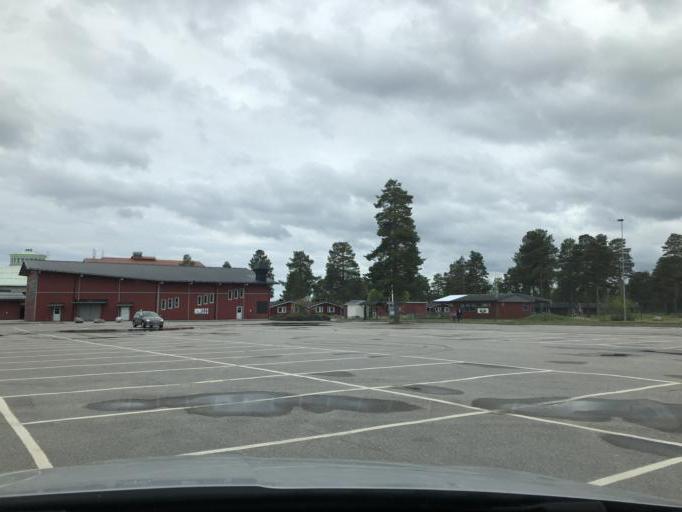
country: SE
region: Norrbotten
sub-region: Pitea Kommun
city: Pitea
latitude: 65.2355
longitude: 21.5305
